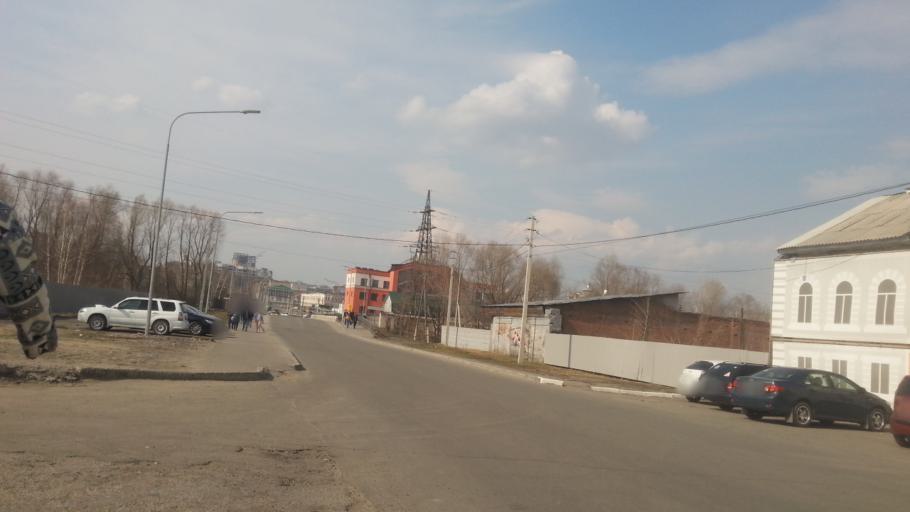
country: RU
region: Altai Krai
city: Zaton
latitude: 53.3268
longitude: 83.7928
